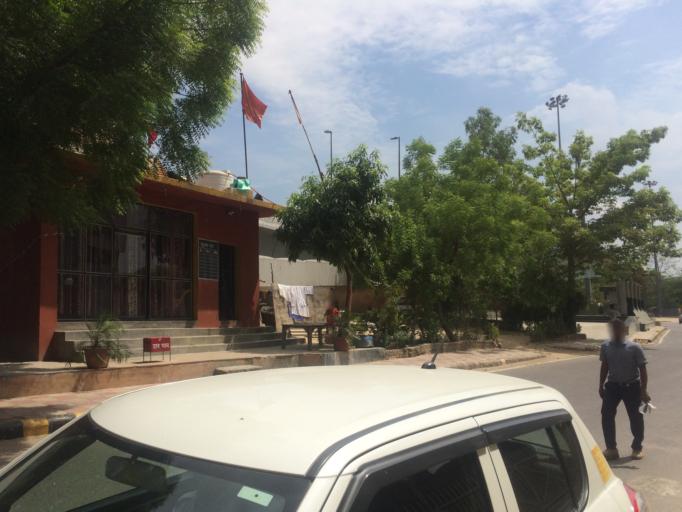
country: IN
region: NCT
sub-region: New Delhi
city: New Delhi
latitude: 28.5847
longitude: 77.2396
